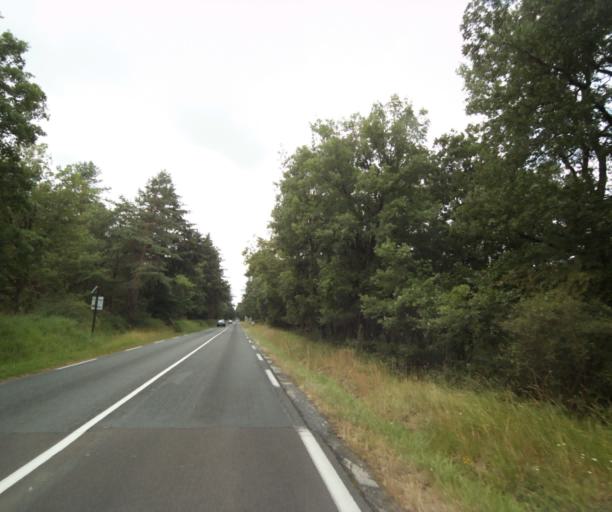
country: FR
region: Ile-de-France
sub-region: Departement de Seine-et-Marne
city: Barbizon
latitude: 48.4160
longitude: 2.6245
